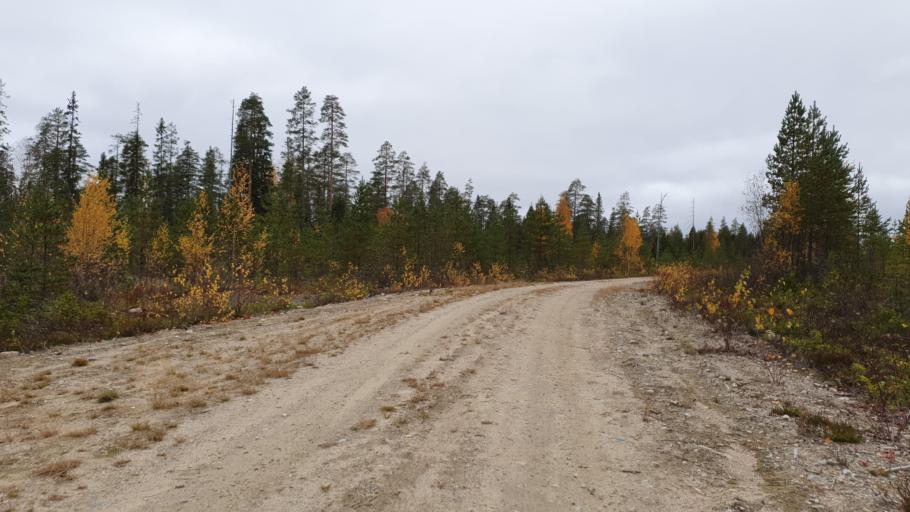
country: FI
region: Kainuu
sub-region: Kehys-Kainuu
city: Kuhmo
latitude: 64.4392
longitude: 29.6246
